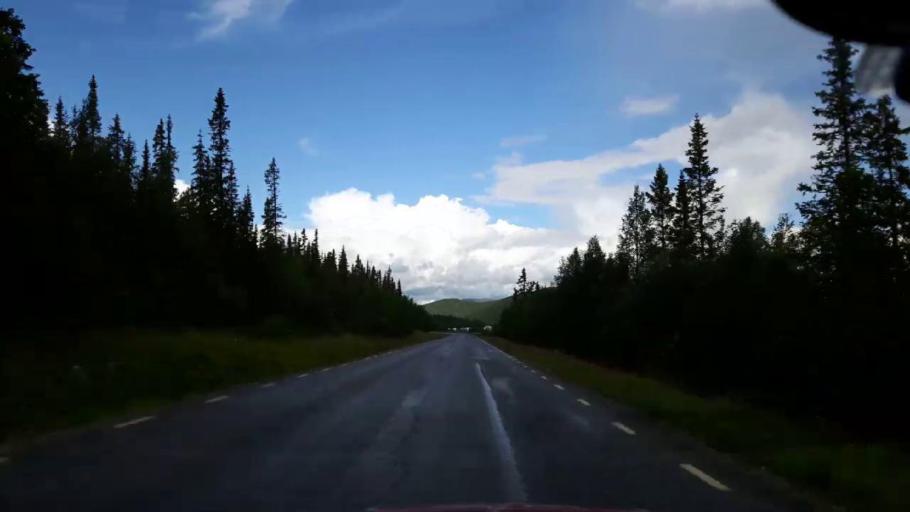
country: SE
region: Vaesterbotten
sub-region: Vilhelmina Kommun
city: Sjoberg
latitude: 65.0054
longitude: 15.1893
